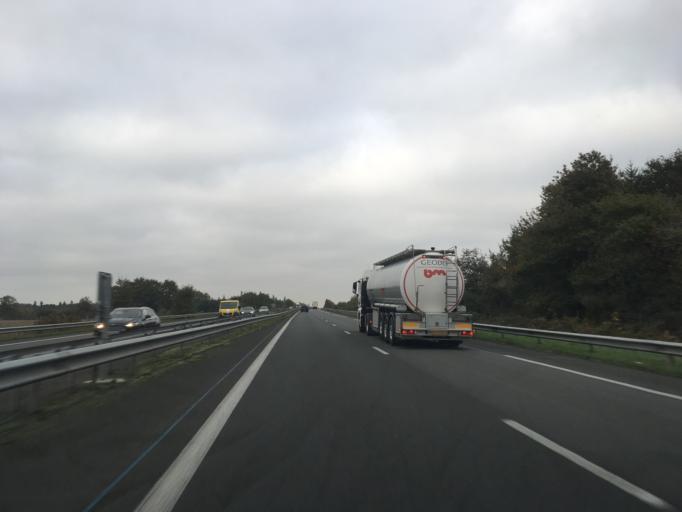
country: FR
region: Pays de la Loire
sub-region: Departement de la Sarthe
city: Parce-sur-Sarthe
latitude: 47.8190
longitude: -0.1554
